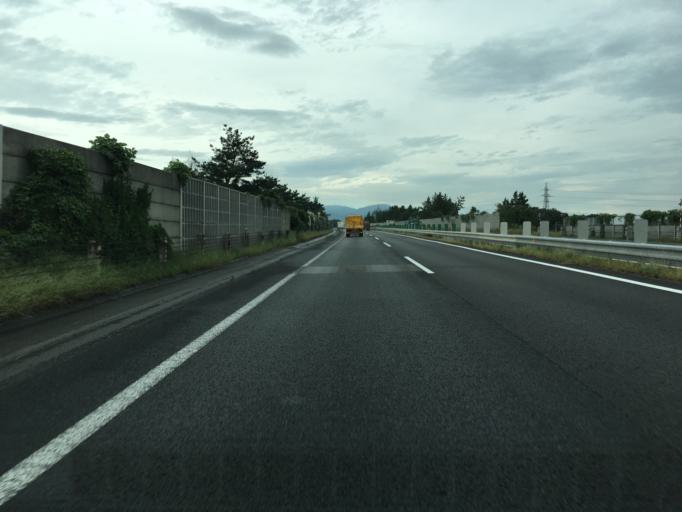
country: JP
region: Fukushima
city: Fukushima-shi
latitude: 37.7640
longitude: 140.4103
